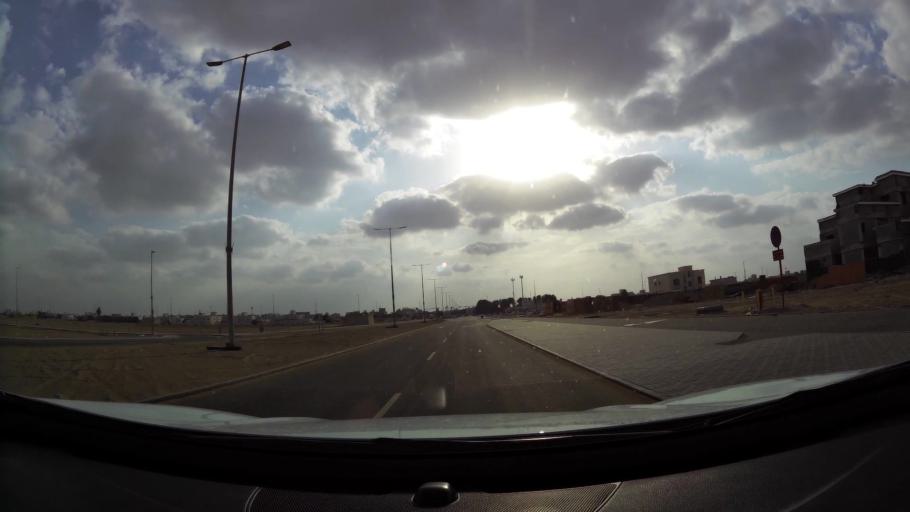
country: AE
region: Abu Dhabi
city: Abu Dhabi
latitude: 24.3404
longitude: 54.5727
